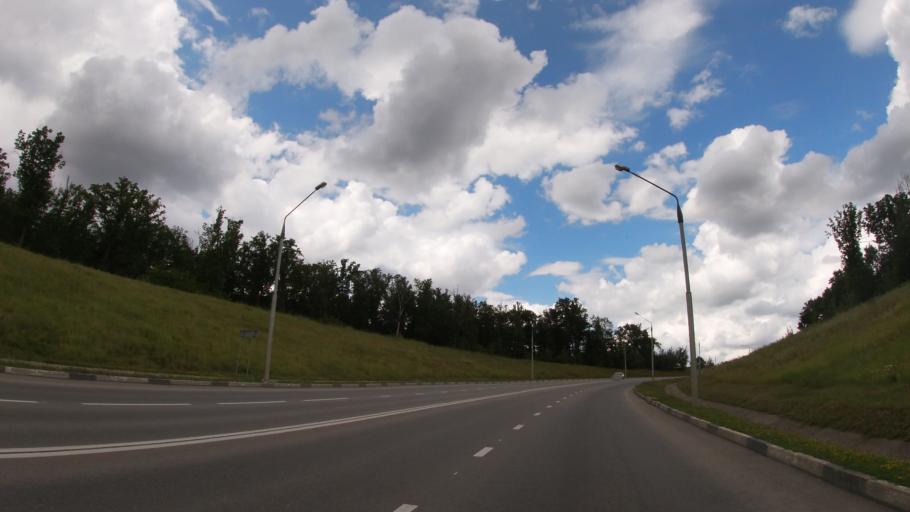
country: RU
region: Belgorod
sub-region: Belgorodskiy Rayon
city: Belgorod
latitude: 50.6233
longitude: 36.6120
